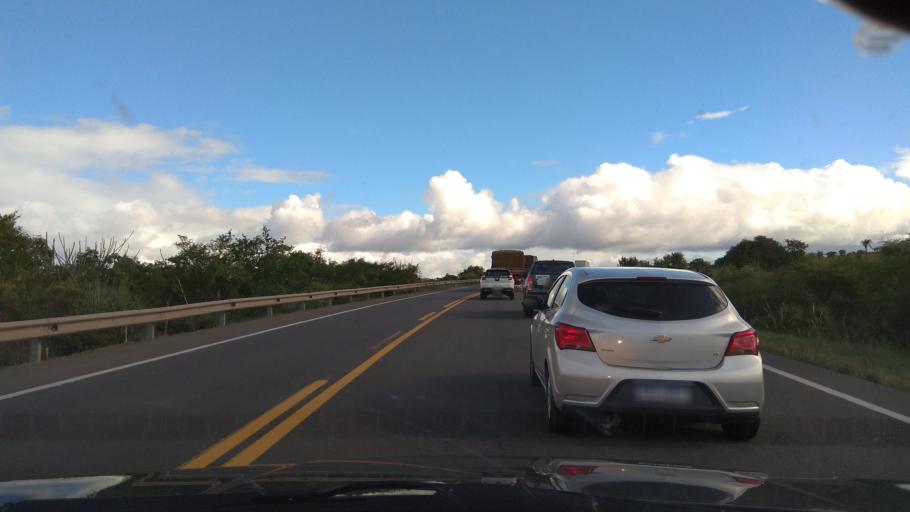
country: BR
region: Bahia
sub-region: Castro Alves
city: Castro Alves
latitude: -12.6480
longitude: -39.6059
